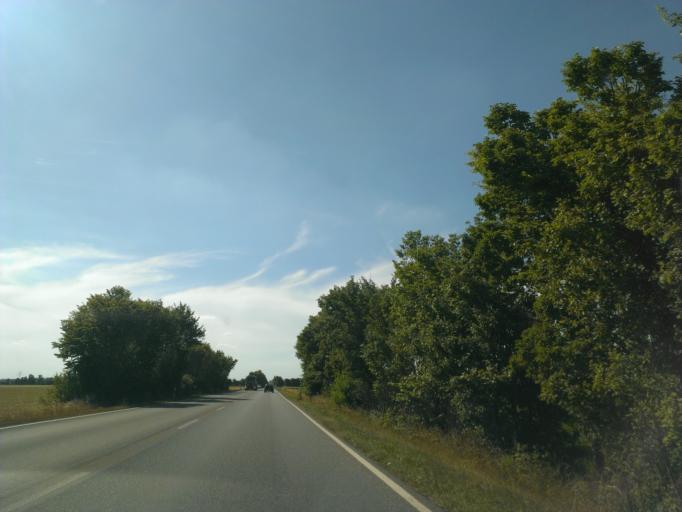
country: DE
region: Bavaria
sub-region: Swabia
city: Reimlingen
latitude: 48.8290
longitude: 10.5412
